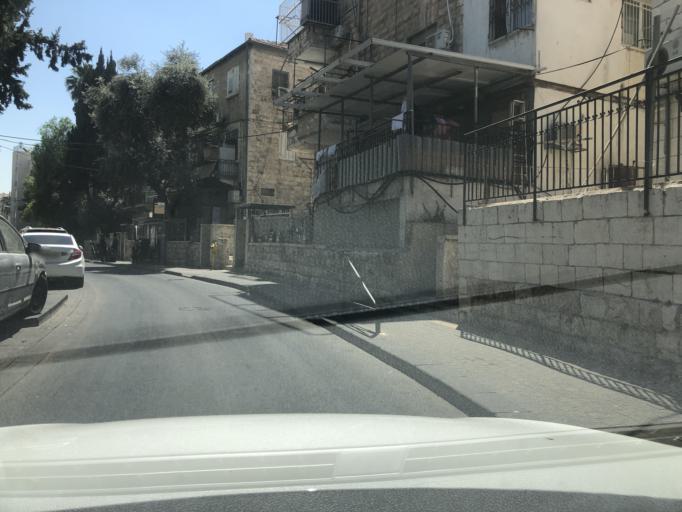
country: IL
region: Jerusalem
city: West Jerusalem
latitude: 31.7923
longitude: 35.2153
